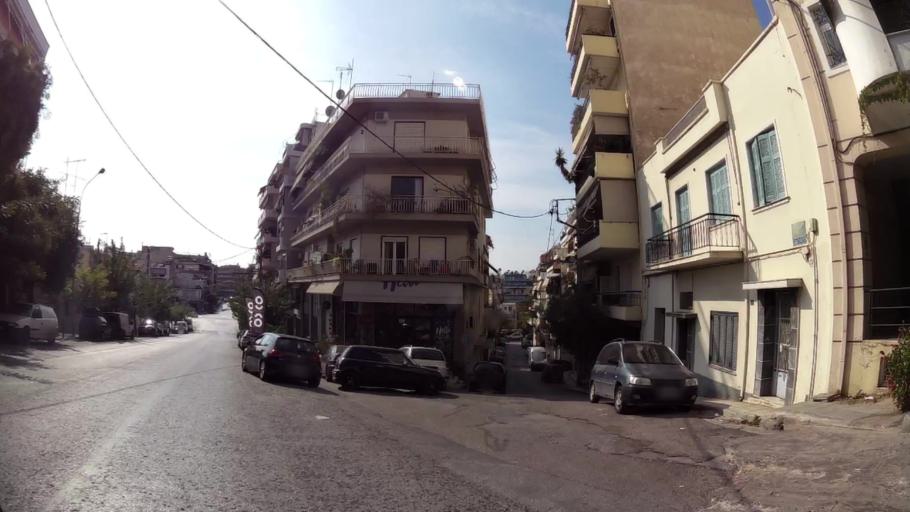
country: GR
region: Attica
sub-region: Nomarchia Athinas
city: Athens
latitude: 37.9646
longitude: 23.7101
